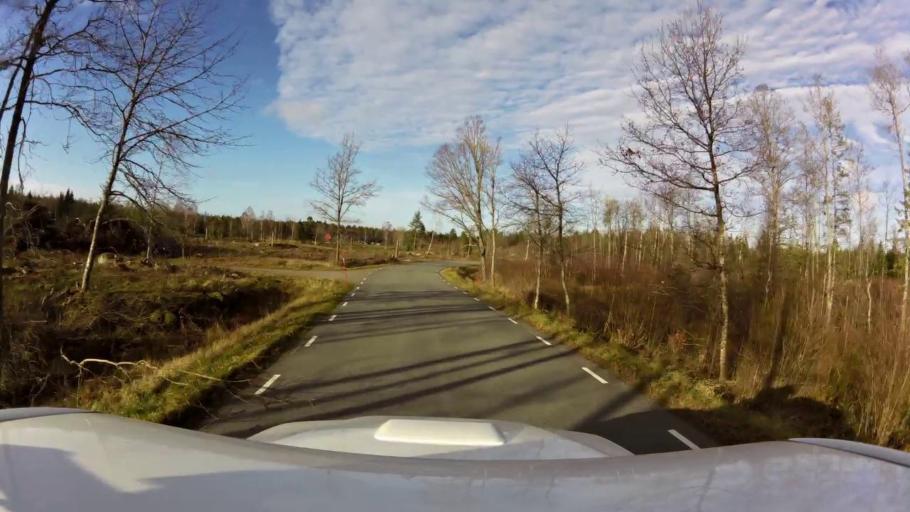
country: SE
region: OEstergoetland
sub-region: Linkopings Kommun
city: Sturefors
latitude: 58.2734
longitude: 15.6633
